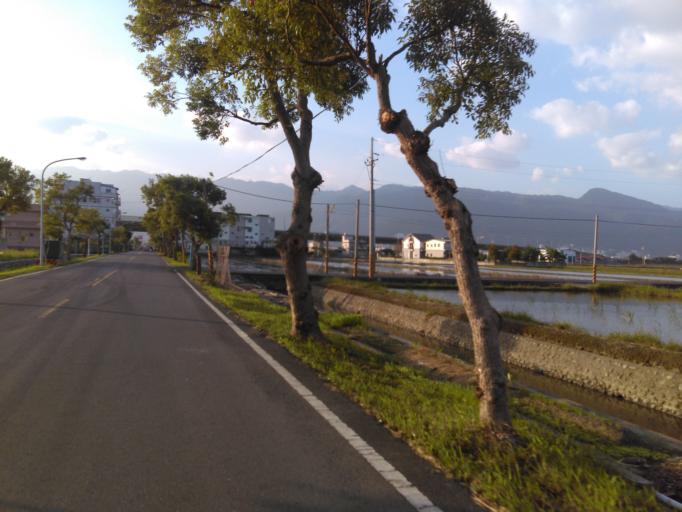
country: TW
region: Taiwan
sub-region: Yilan
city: Yilan
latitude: 24.7995
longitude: 121.7850
